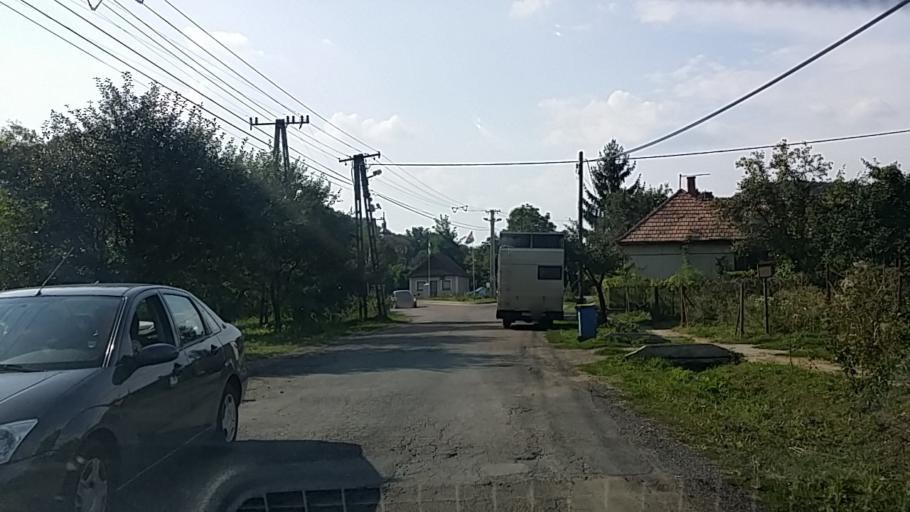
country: HU
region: Nograd
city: Bujak
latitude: 47.8645
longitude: 19.5040
